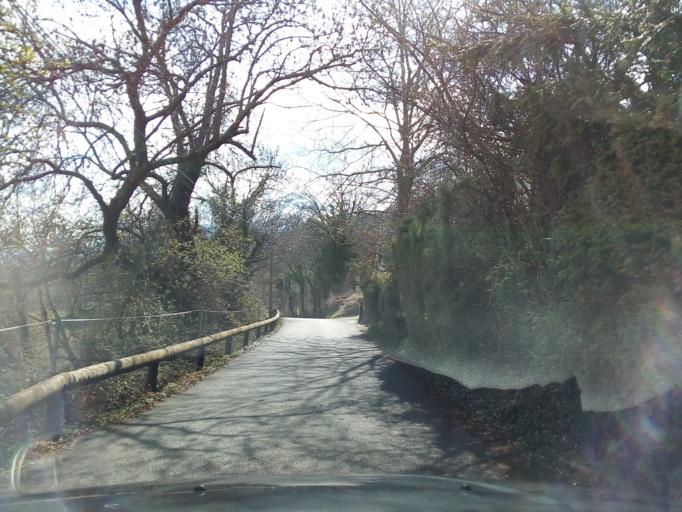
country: FR
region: Rhone-Alpes
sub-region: Departement de la Savoie
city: Saint-Baldoph
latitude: 45.5291
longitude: 5.9486
